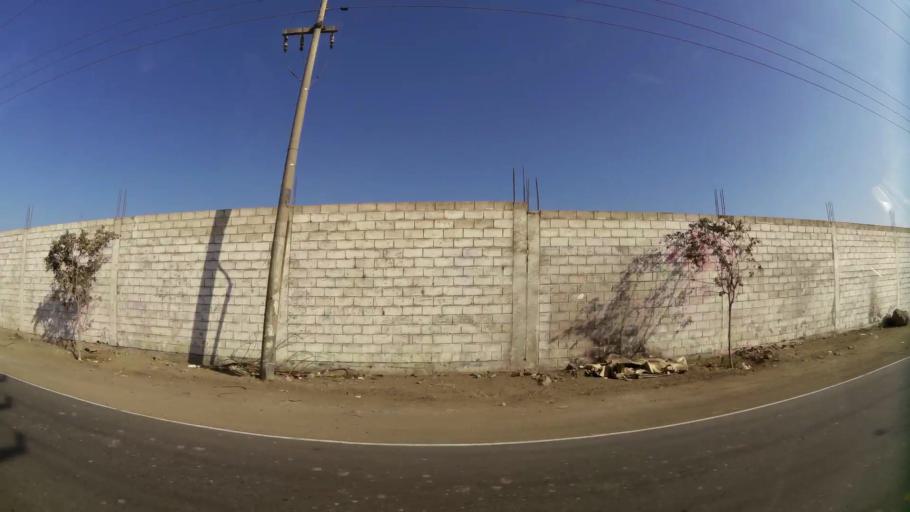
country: PE
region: Ica
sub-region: Provincia de Chincha
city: Chincha Baja
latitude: -13.4508
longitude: -76.1413
